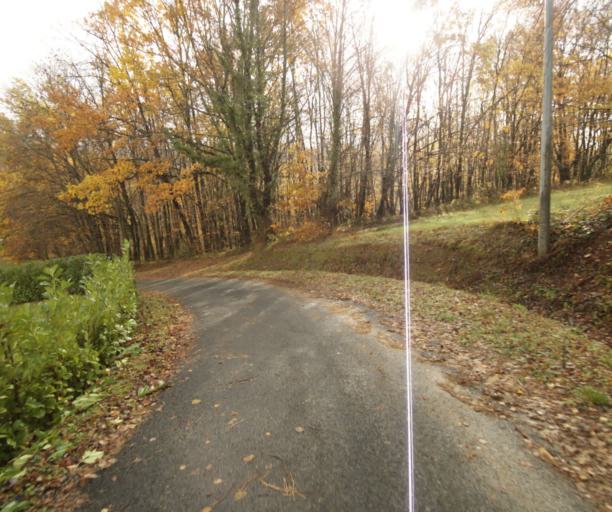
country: FR
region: Limousin
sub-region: Departement de la Correze
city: Cornil
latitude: 45.1979
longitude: 1.6520
